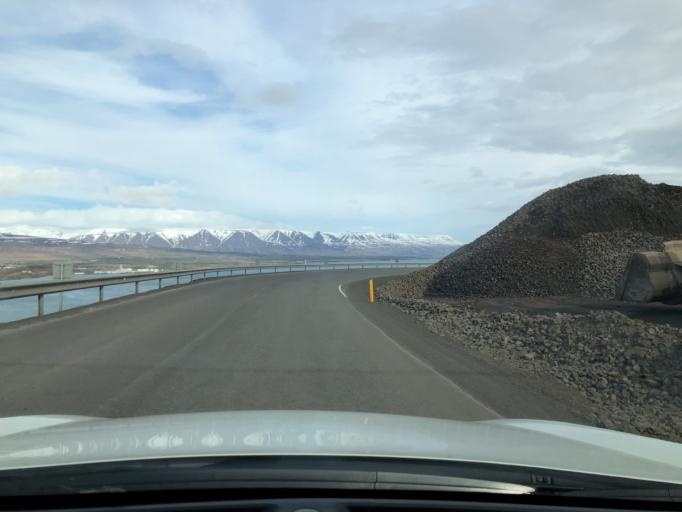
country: IS
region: Northeast
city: Akureyri
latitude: 65.6903
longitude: -18.0533
